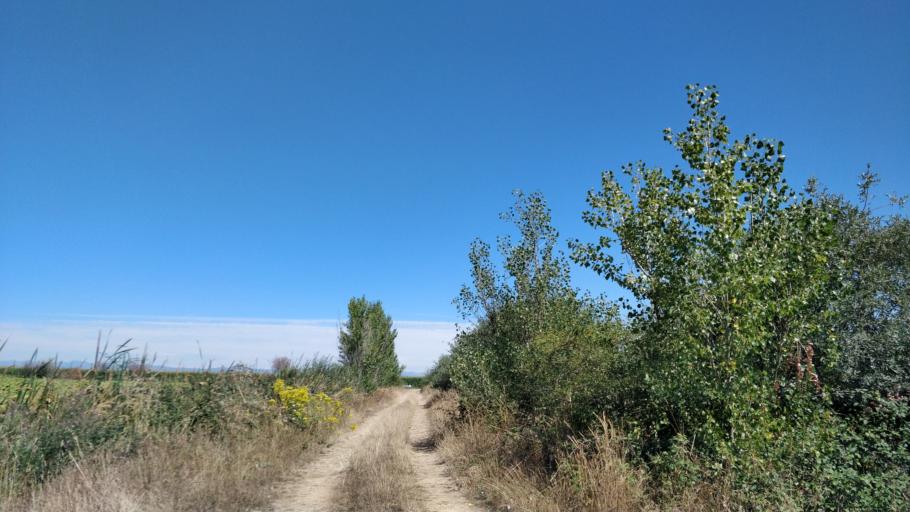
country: ES
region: Castille and Leon
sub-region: Provincia de Leon
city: Bustillo del Paramo
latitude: 42.4507
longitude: -5.8170
